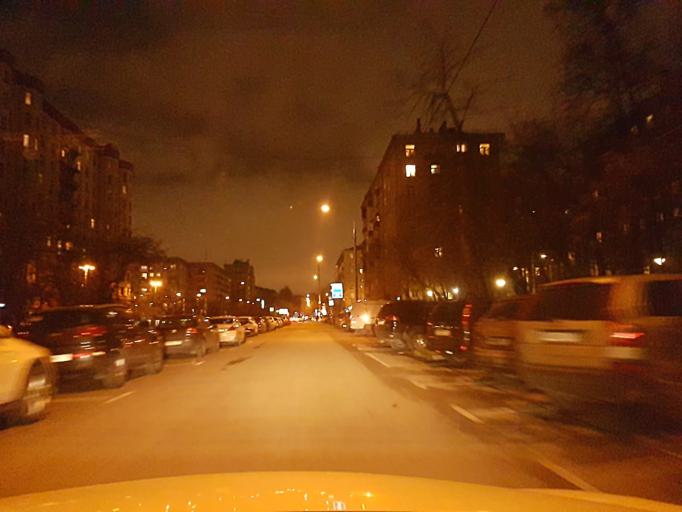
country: RU
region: Moscow
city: Novyye Cheremushki
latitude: 55.7213
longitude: 37.5777
